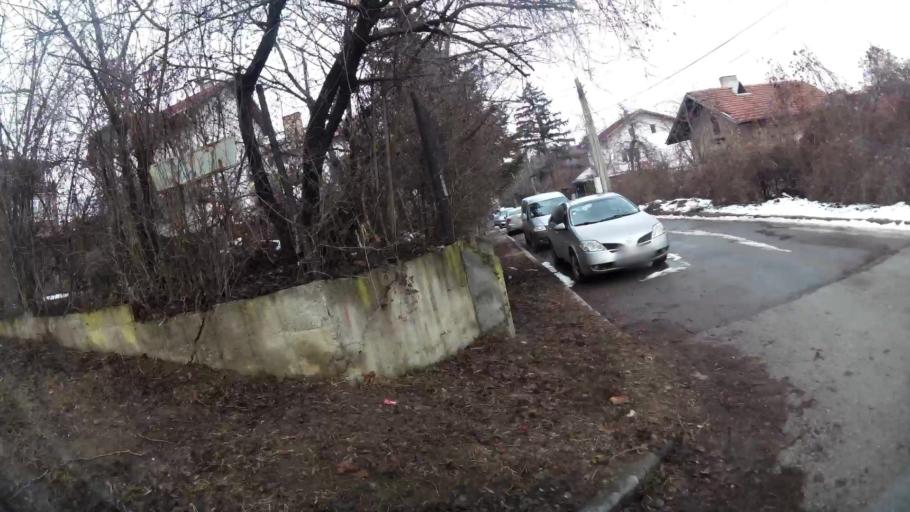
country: BG
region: Sofia-Capital
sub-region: Stolichna Obshtina
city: Sofia
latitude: 42.6649
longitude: 23.2417
